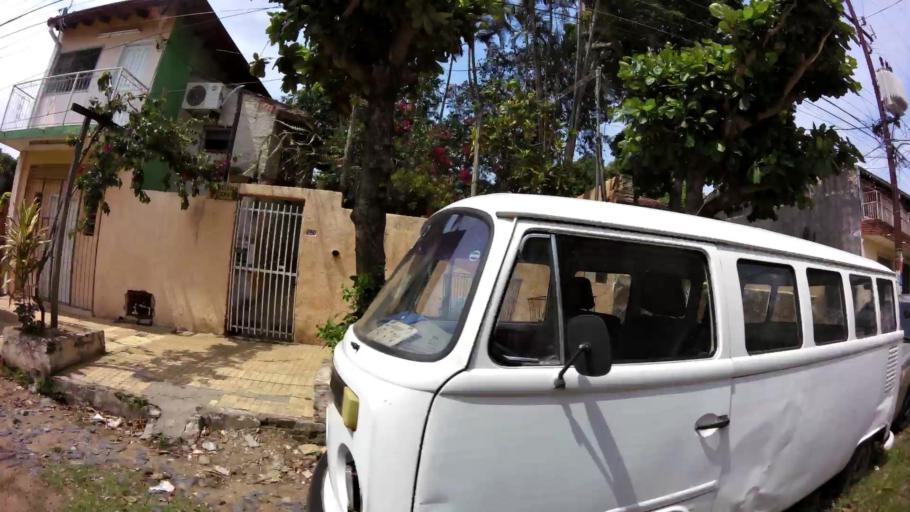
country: PY
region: Asuncion
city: Asuncion
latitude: -25.2659
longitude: -57.5916
